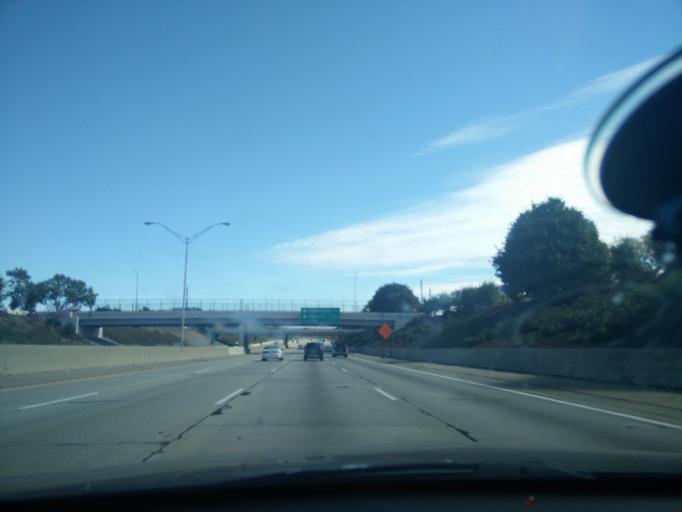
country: US
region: Michigan
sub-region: Macomb County
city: Center Line
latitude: 42.4919
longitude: -83.0098
